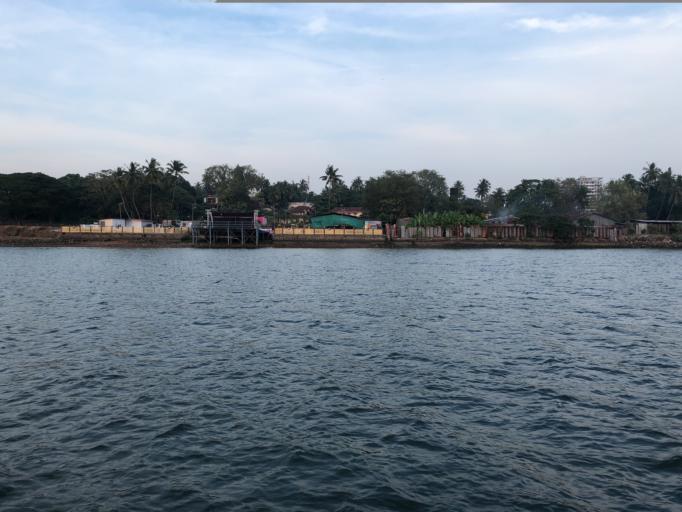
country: IN
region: Karnataka
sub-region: Dakshina Kannada
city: Ullal
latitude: 12.8440
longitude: 74.8393
